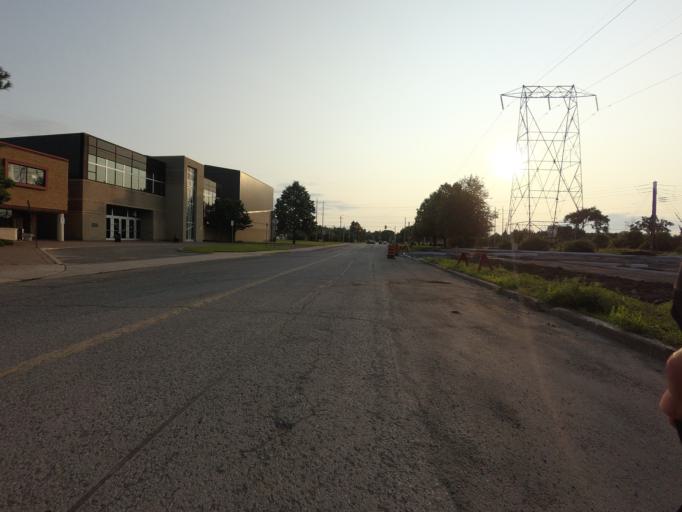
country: CA
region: Ontario
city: Bells Corners
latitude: 45.3271
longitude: -75.7785
